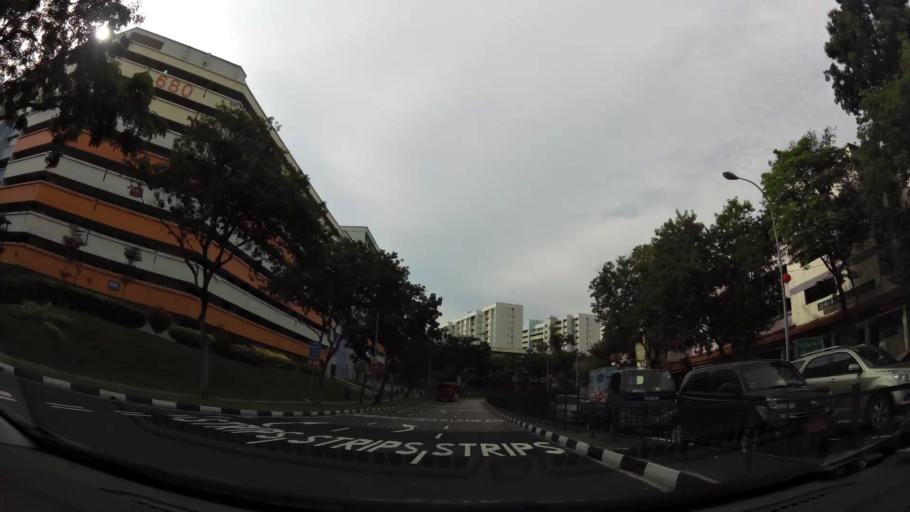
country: SG
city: Singapore
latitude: 1.3722
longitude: 103.8857
